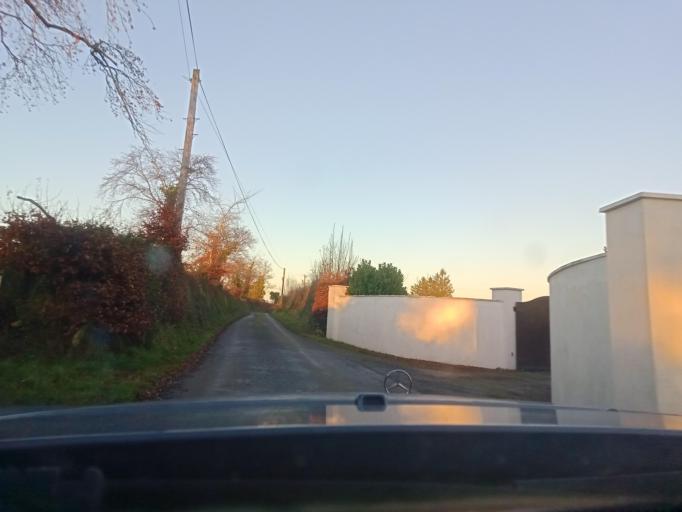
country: IE
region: Leinster
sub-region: Kilkenny
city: Graiguenamanagh
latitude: 52.4808
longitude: -6.9388
